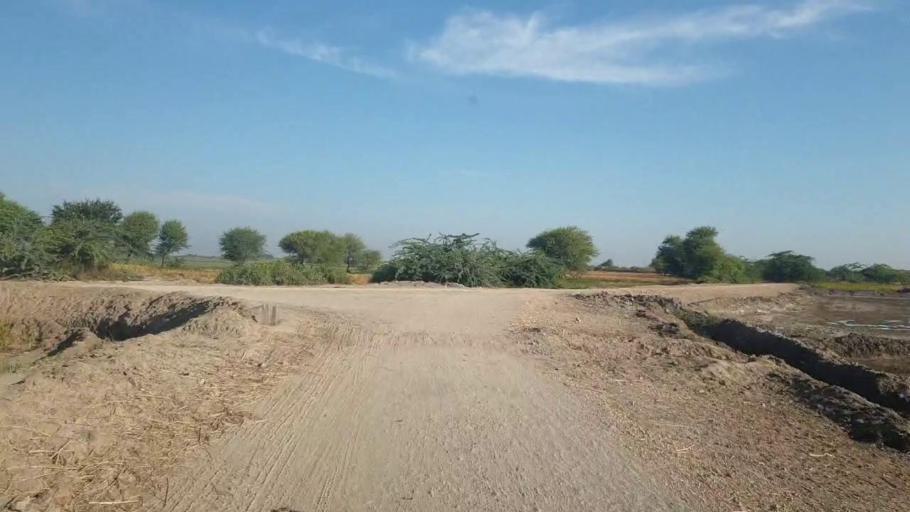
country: PK
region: Sindh
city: Talhar
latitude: 24.8241
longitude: 68.8396
